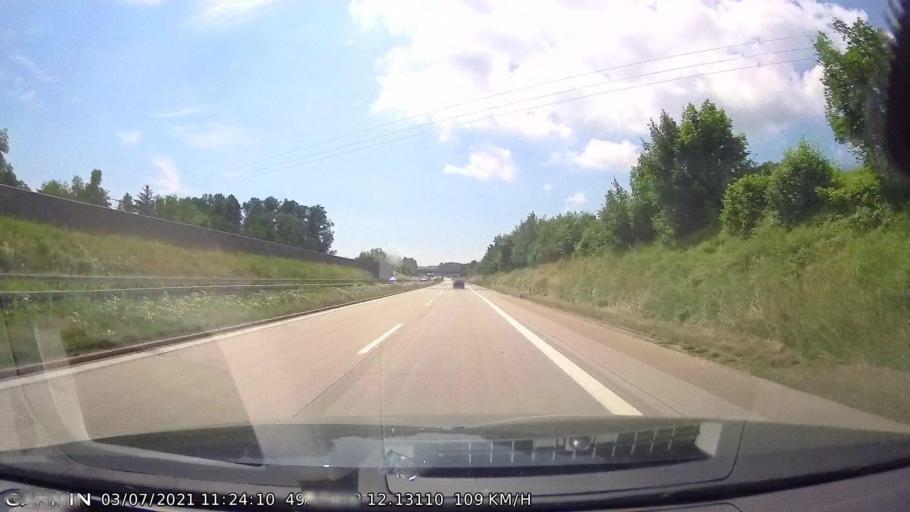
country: DE
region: Bavaria
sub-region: Upper Palatinate
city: Wernberg-Koblitz
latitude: 49.5422
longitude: 12.1312
